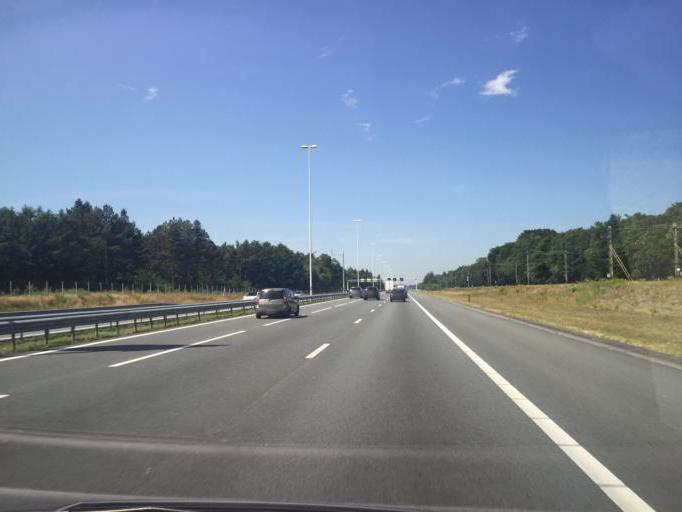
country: NL
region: Utrecht
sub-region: Gemeente Utrechtse Heuvelrug
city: Doorn
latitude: 52.0655
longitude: 5.3223
